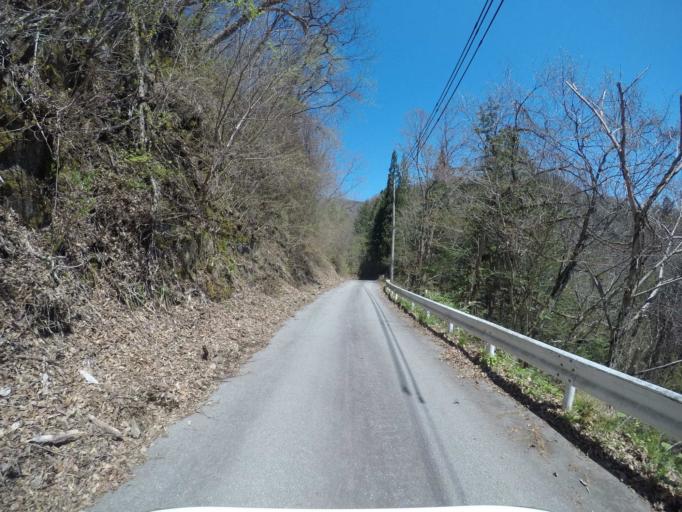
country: JP
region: Gifu
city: Takayama
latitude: 36.1667
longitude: 137.4387
